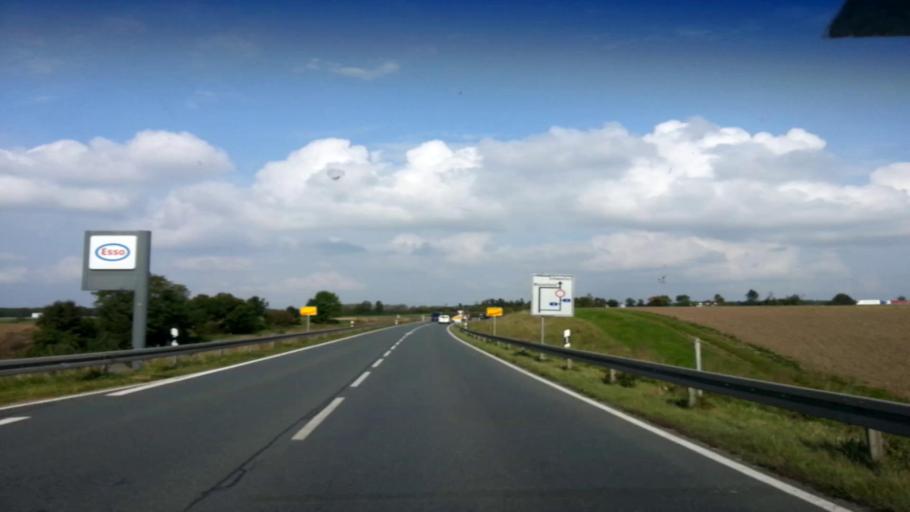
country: DE
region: Bavaria
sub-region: Regierungsbezirk Unterfranken
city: Castell
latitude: 49.7710
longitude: 10.3411
